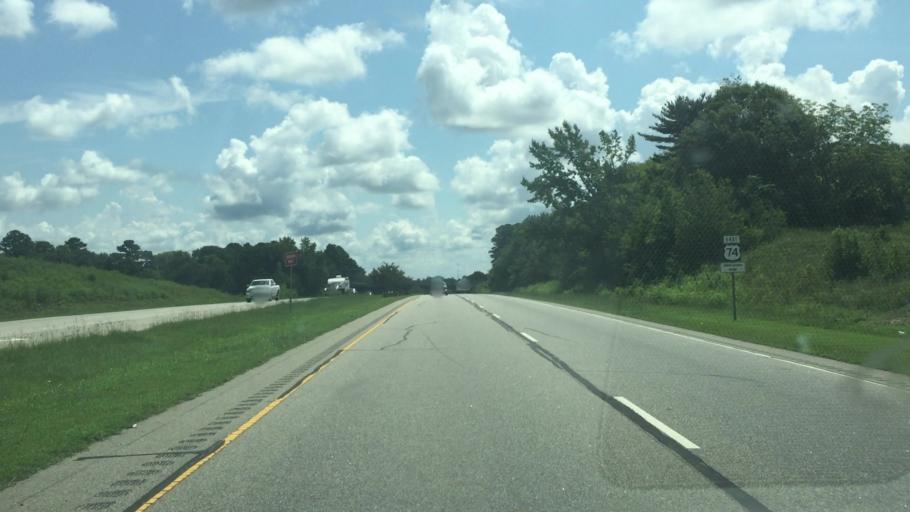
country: US
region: North Carolina
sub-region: Anson County
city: Wadesboro
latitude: 34.9624
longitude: -79.9902
